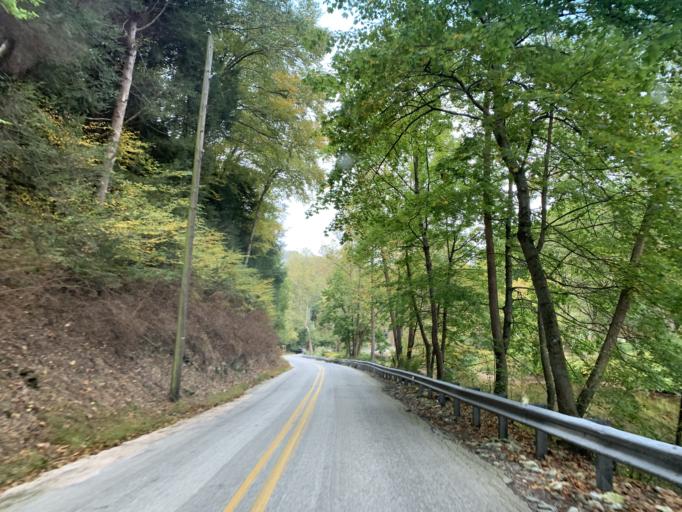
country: US
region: Pennsylvania
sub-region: York County
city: Susquehanna Trails
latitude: 39.7902
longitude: -76.4202
